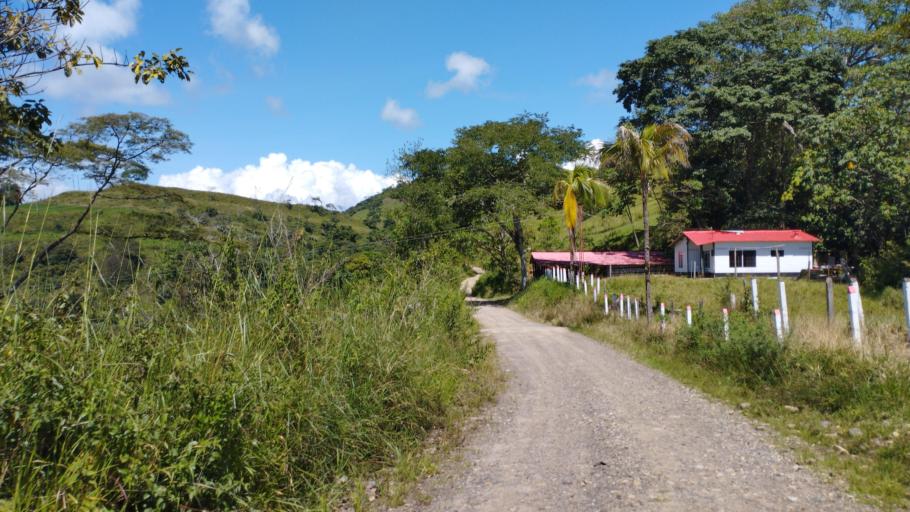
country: CO
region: Boyaca
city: San Luis de Gaceno
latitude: 4.7932
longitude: -73.1085
